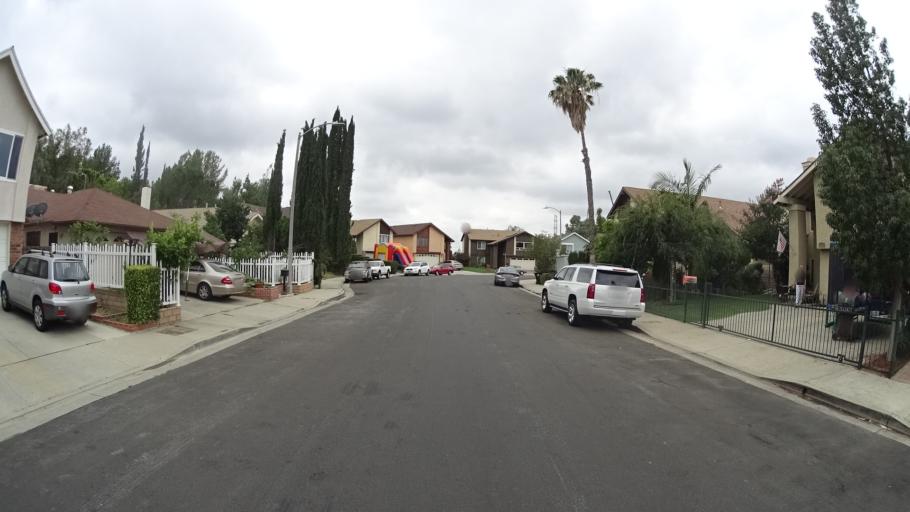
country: US
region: California
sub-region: Los Angeles County
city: San Fernando
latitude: 34.2772
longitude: -118.4584
